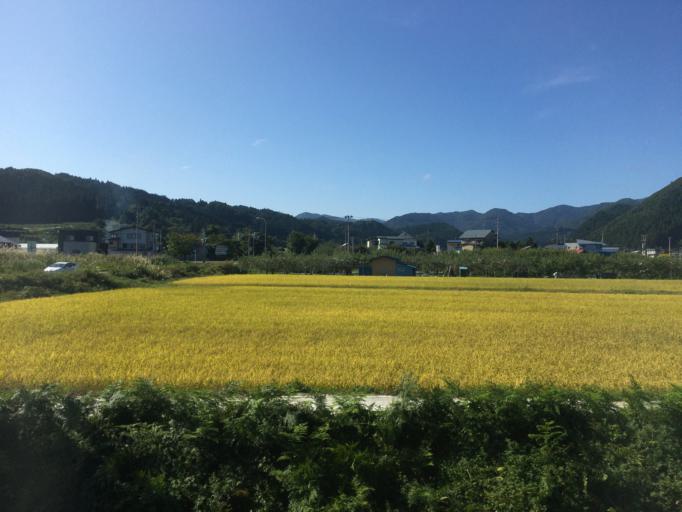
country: JP
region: Aomori
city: Hirosaki
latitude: 40.5250
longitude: 140.5539
